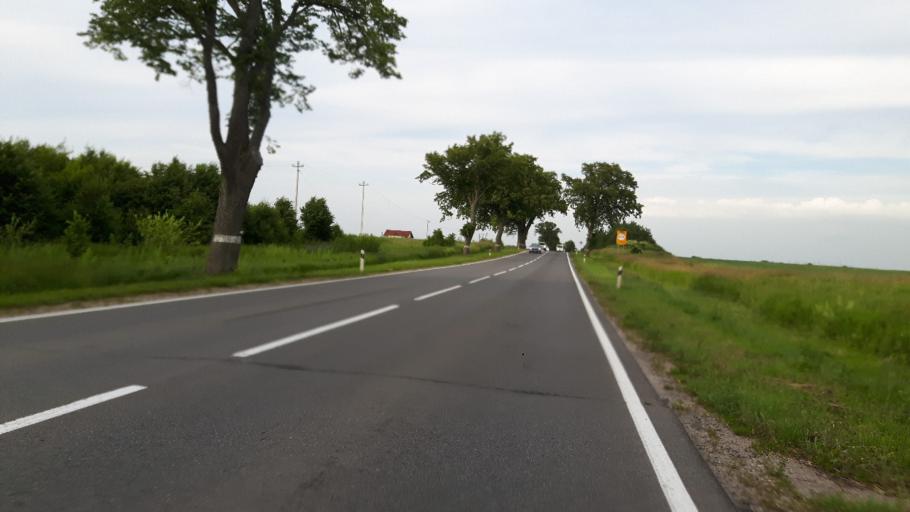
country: RU
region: Kaliningrad
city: Vzmorye
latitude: 54.6258
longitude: 20.2913
